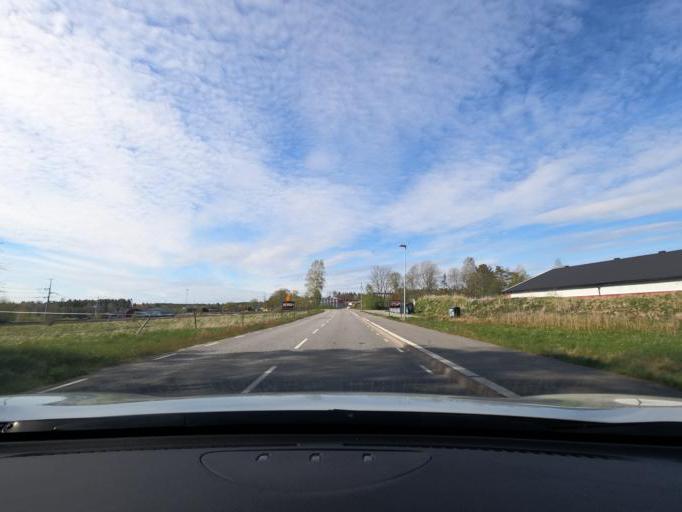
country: SE
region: Vaestra Goetaland
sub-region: Harryda Kommun
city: Landvetter
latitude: 57.6736
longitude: 12.2436
